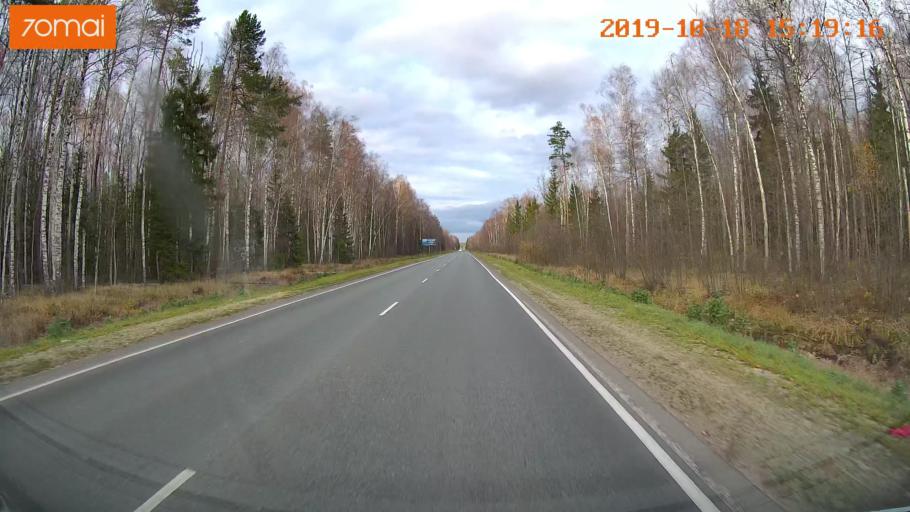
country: RU
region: Vladimir
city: Anopino
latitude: 55.6706
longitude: 40.7364
